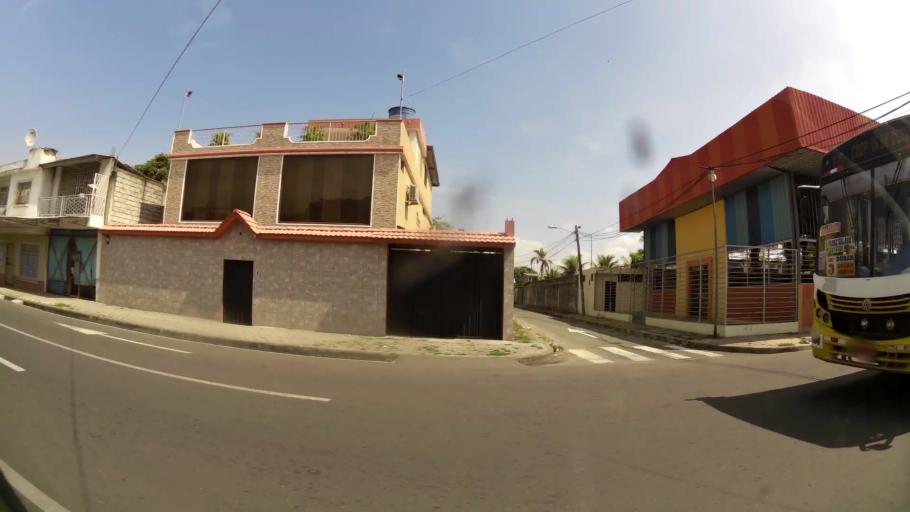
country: EC
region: Guayas
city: Eloy Alfaro
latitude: -2.1585
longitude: -79.8417
